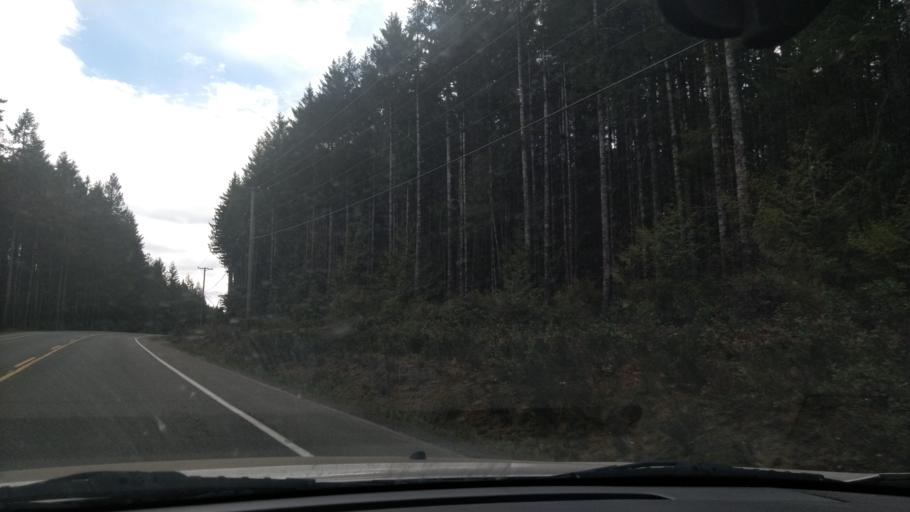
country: CA
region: British Columbia
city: Campbell River
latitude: 50.0212
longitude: -125.3533
